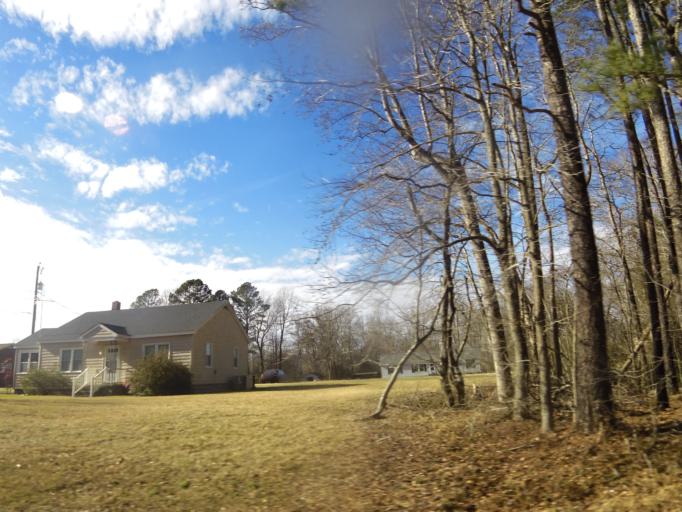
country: US
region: Virginia
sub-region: City of Franklin
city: Franklin
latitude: 36.7503
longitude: -76.8706
